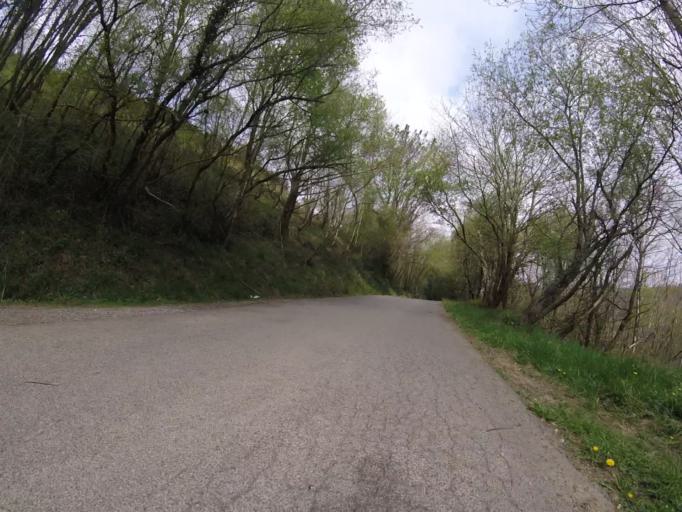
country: ES
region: Basque Country
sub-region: Provincia de Guipuzcoa
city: Asteasu
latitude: 43.2181
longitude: -2.0910
